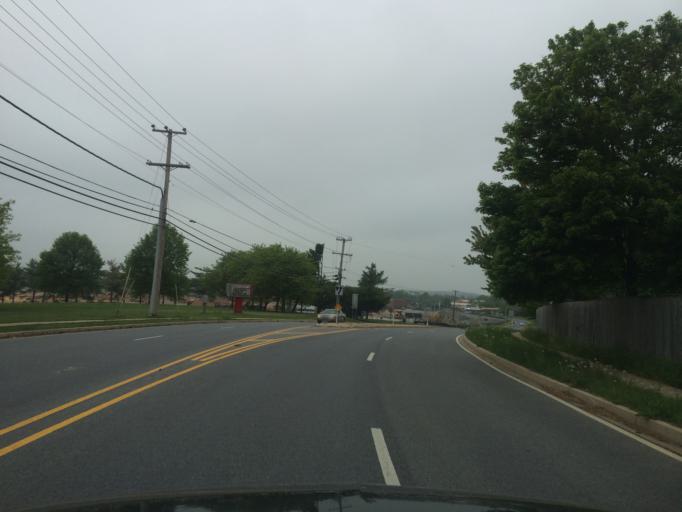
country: US
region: Maryland
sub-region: Carroll County
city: Eldersburg
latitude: 39.3940
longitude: -76.9323
